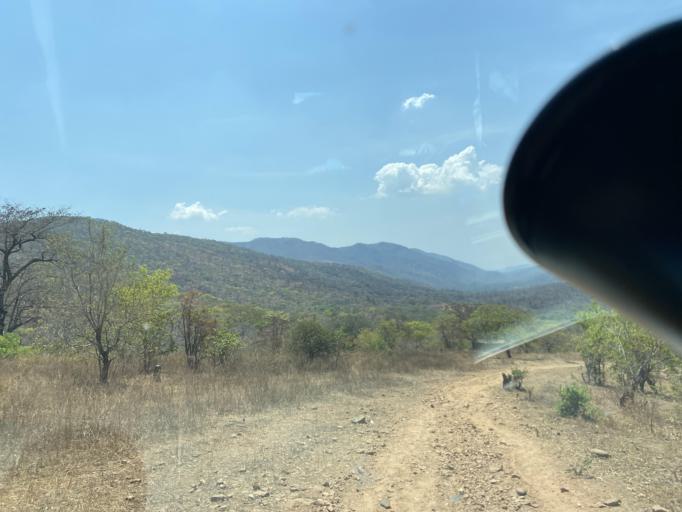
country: ZM
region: Lusaka
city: Kafue
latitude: -15.7963
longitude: 28.4562
